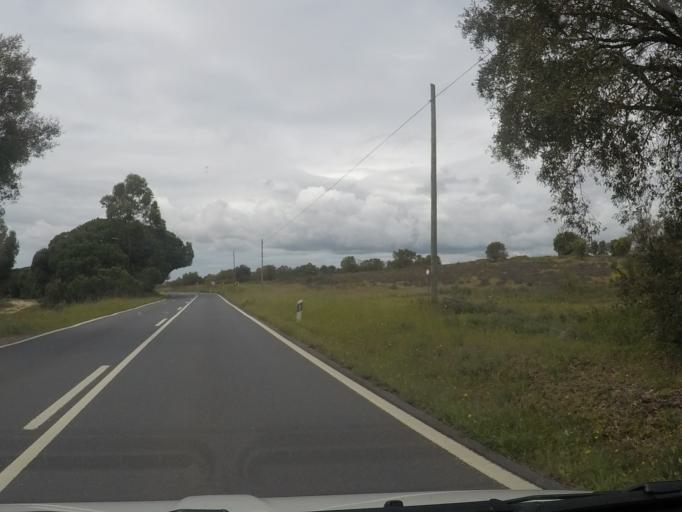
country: PT
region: Setubal
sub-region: Sines
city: Porto Covo
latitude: 37.8785
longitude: -8.7442
